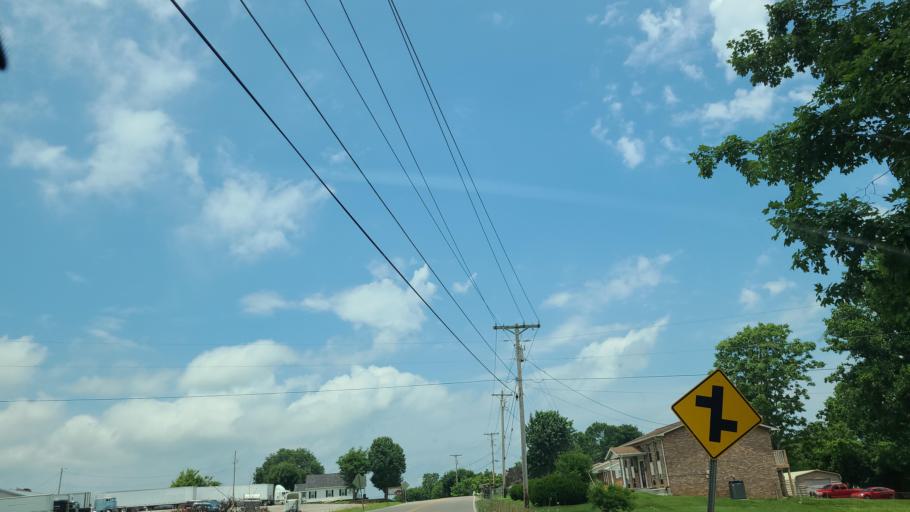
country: US
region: Tennessee
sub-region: Hamblen County
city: Morristown
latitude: 36.1645
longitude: -83.3613
